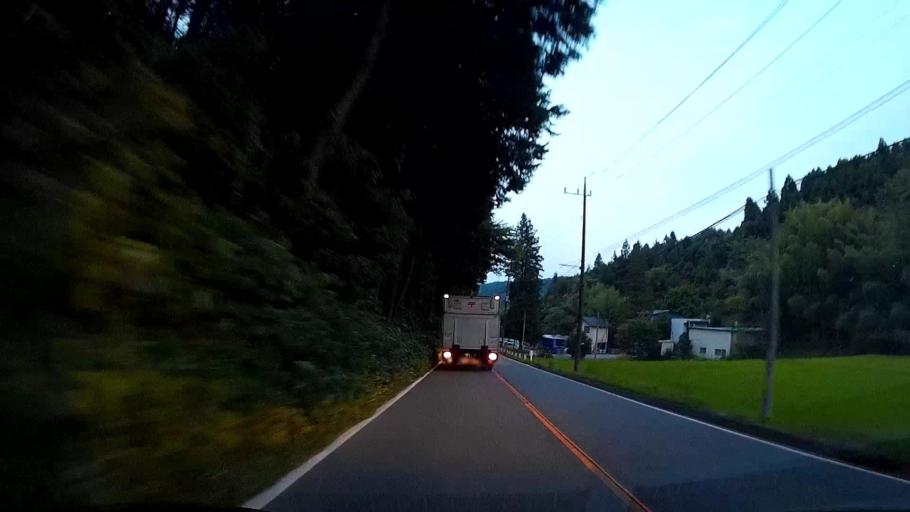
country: JP
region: Gunma
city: Annaka
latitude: 36.3880
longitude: 138.8558
